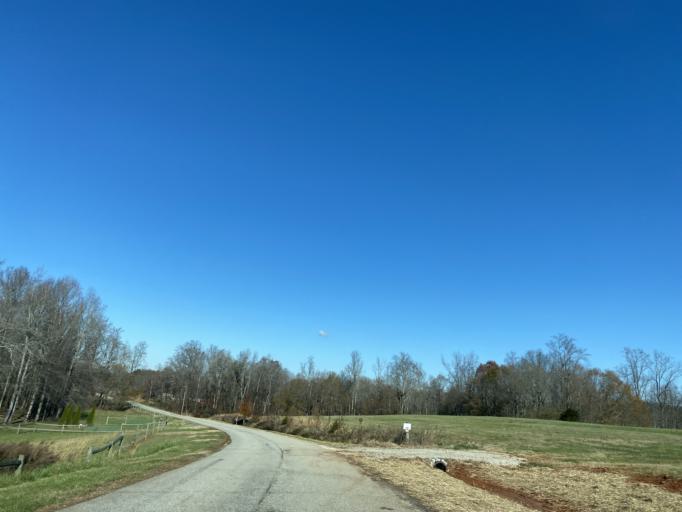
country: US
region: South Carolina
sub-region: Spartanburg County
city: Mayo
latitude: 35.1415
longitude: -81.7846
